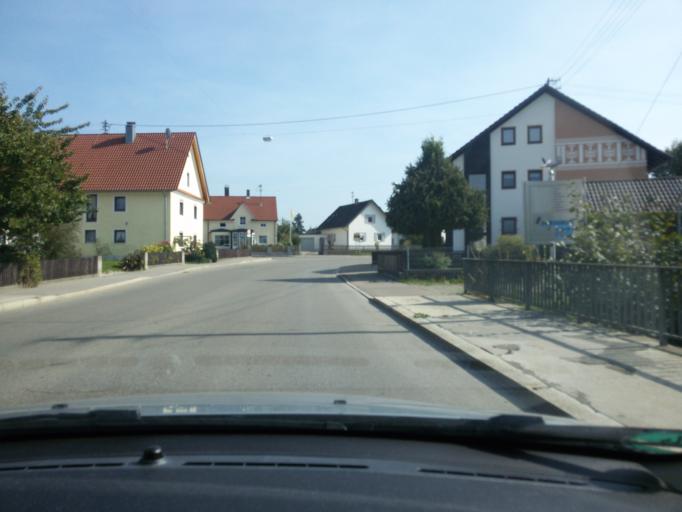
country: DE
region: Bavaria
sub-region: Swabia
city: Ziemetshausen
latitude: 48.2929
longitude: 10.5340
